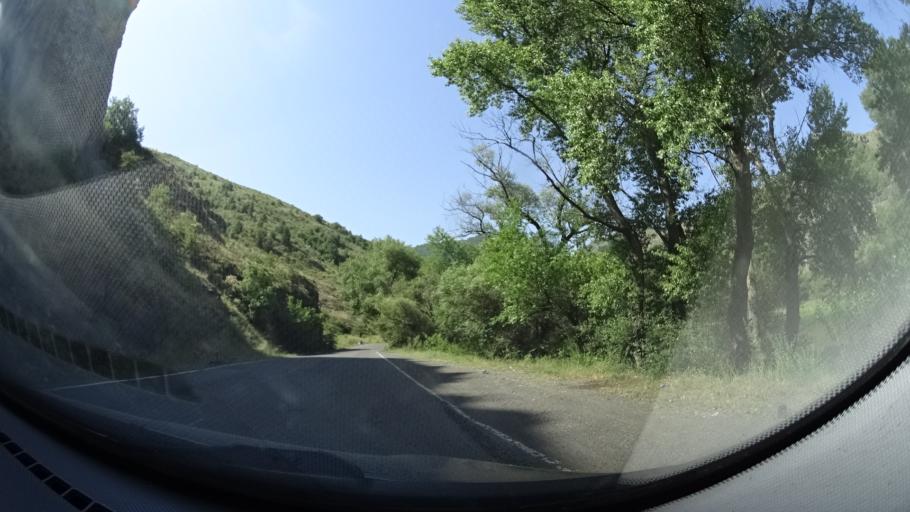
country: GE
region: Samtskhe-Javakheti
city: Akhaltsikhe
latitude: 41.6203
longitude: 43.0692
